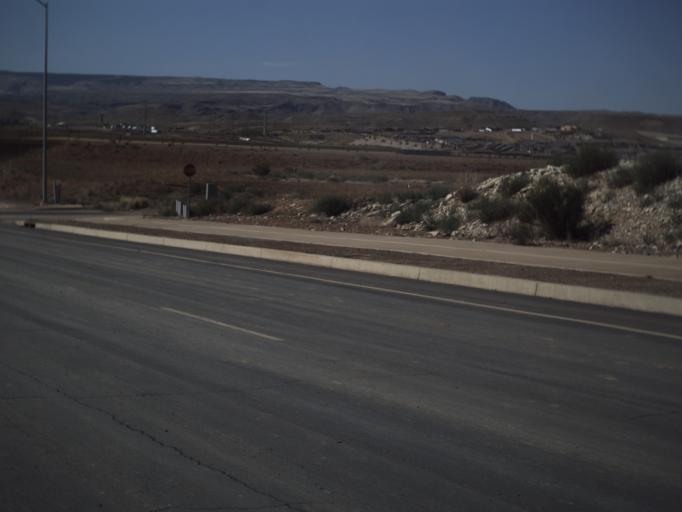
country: US
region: Utah
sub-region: Washington County
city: Saint George
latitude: 37.0269
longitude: -113.6009
